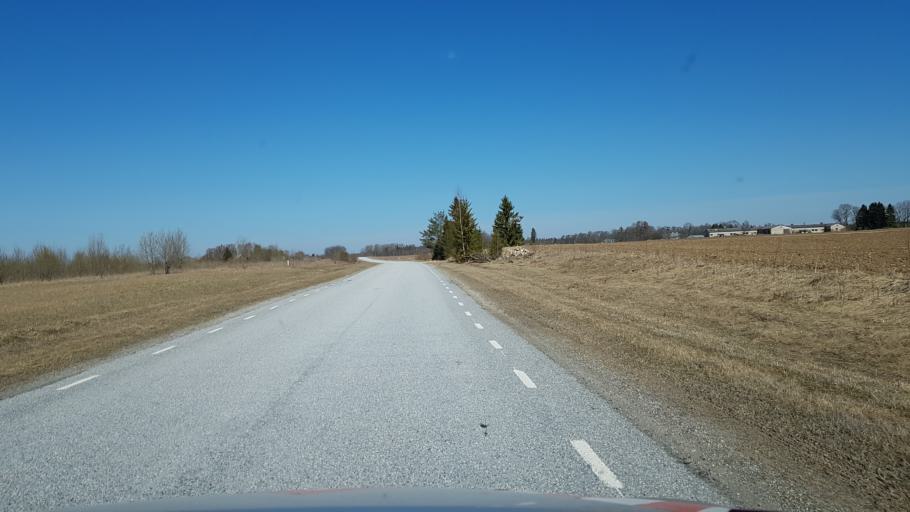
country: EE
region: Jaervamaa
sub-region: Koeru vald
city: Koeru
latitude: 59.0297
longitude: 26.0902
